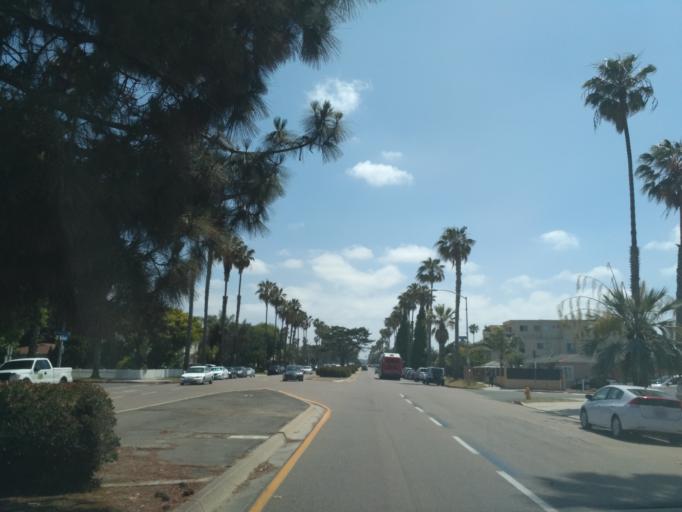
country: US
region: California
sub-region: San Diego County
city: La Jolla
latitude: 32.7957
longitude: -117.2500
